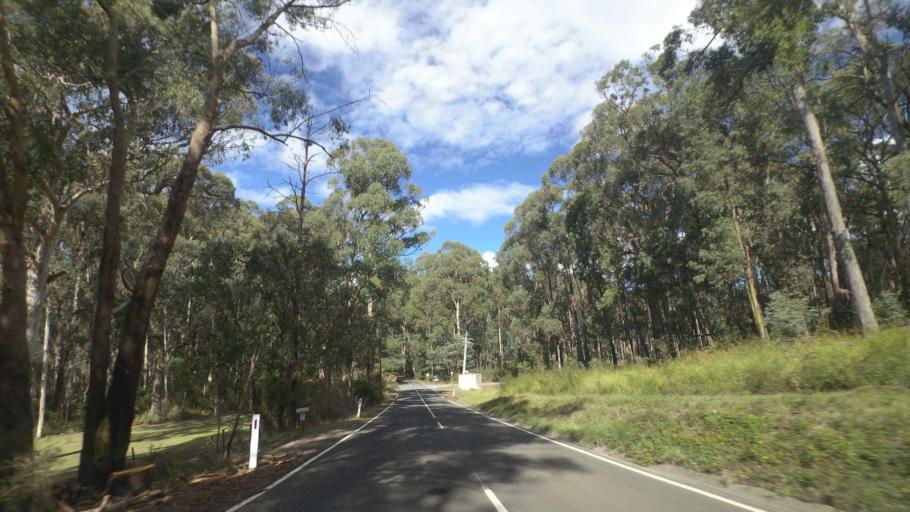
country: AU
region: Victoria
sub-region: Cardinia
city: Gembrook
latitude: -37.9817
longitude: 145.5870
